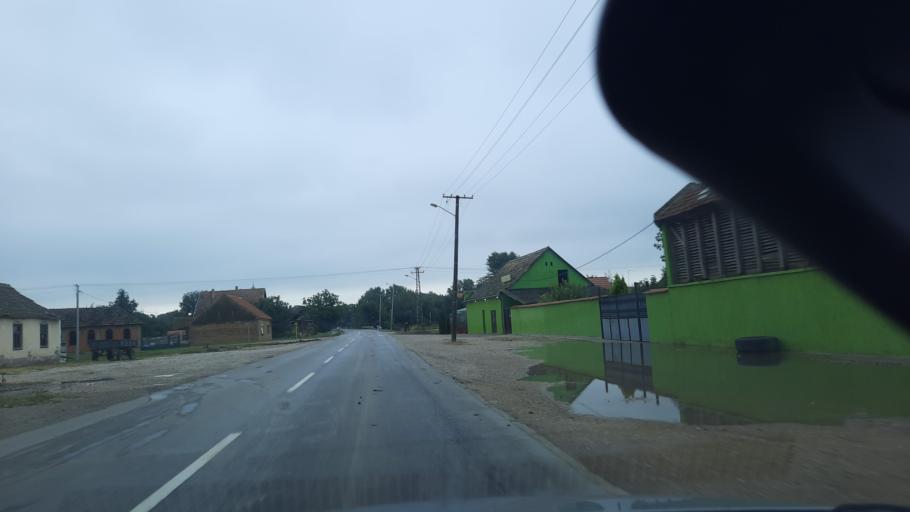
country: RS
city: Farkazdin
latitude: 45.1904
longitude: 20.4685
